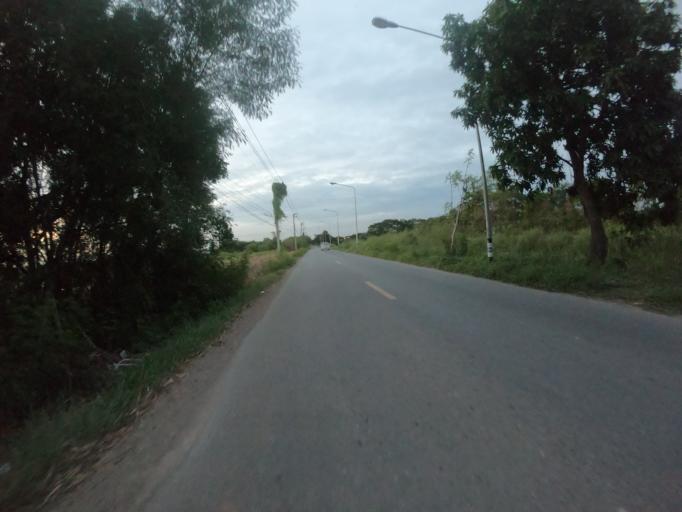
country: TH
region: Pathum Thani
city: Ban Rangsit
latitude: 14.0319
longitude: 100.8005
